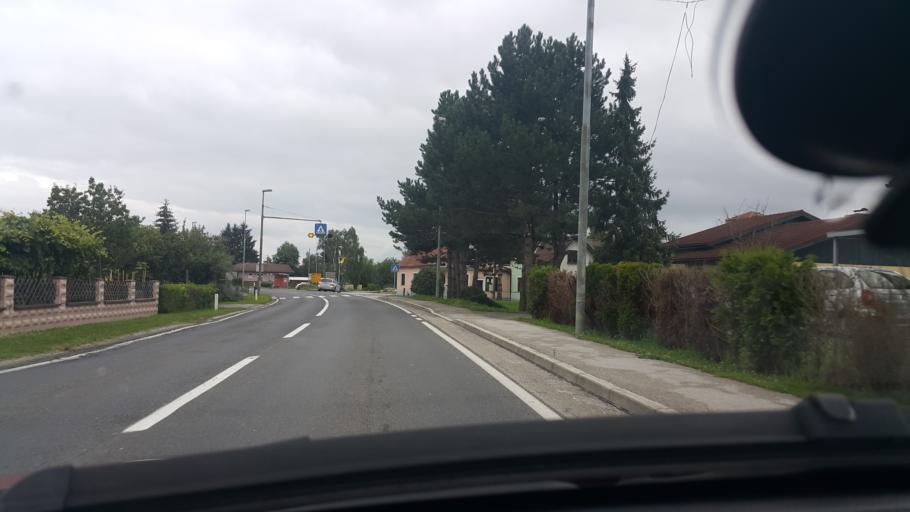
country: SI
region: Gorisnica
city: Gorisnica
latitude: 46.4124
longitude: 16.0123
